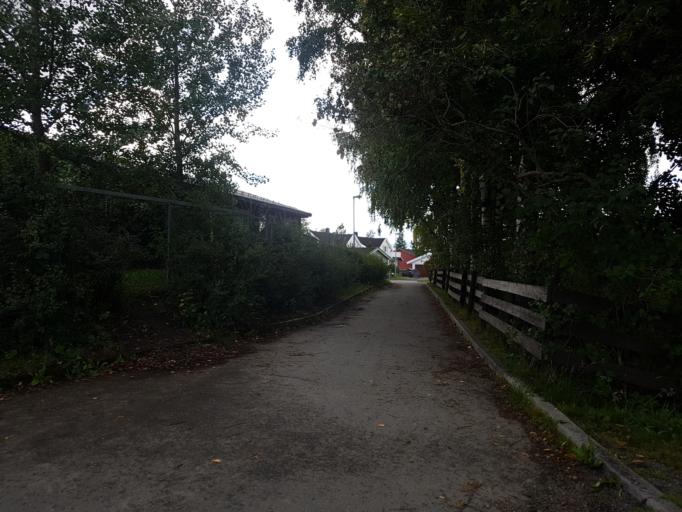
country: NO
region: Sor-Trondelag
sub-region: Trondheim
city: Trondheim
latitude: 63.4114
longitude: 10.4506
